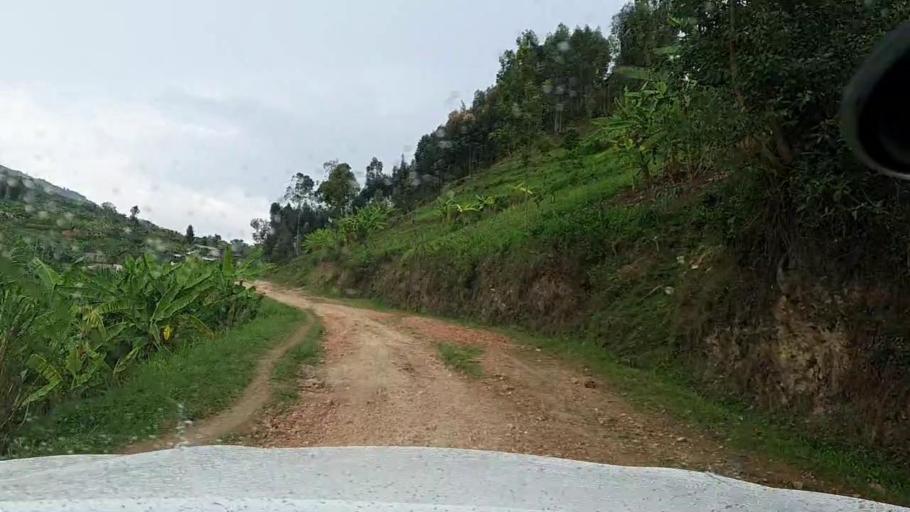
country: RW
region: Western Province
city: Kibuye
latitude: -2.0763
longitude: 29.4395
